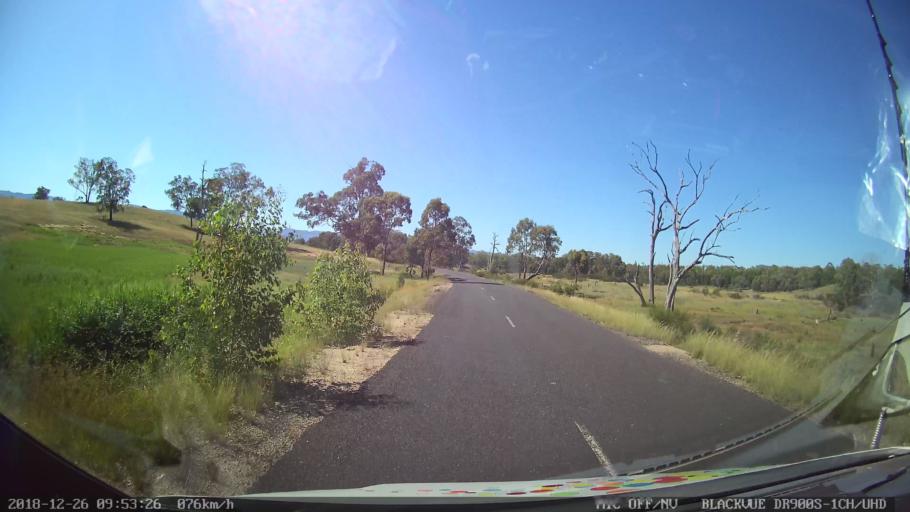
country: AU
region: New South Wales
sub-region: Mid-Western Regional
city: Kandos
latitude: -33.0207
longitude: 150.1535
